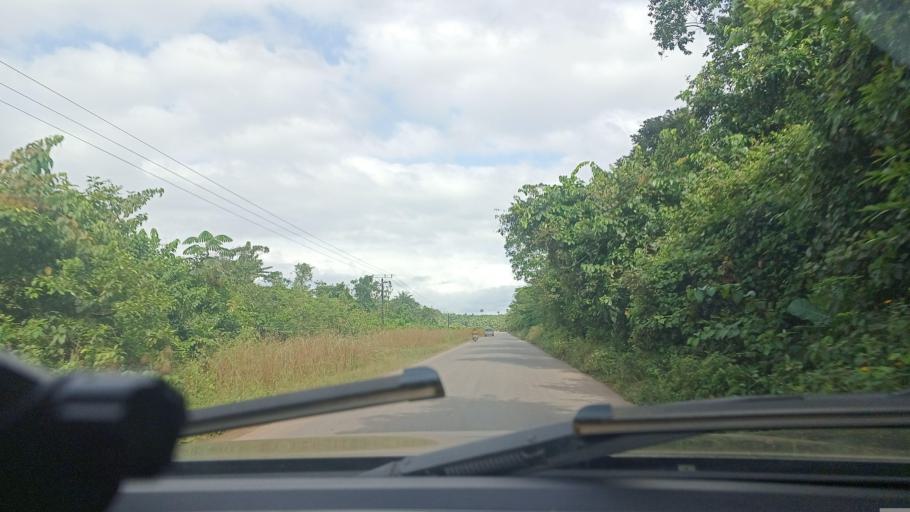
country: LR
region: Bomi
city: Tubmanburg
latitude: 6.7281
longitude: -10.9882
